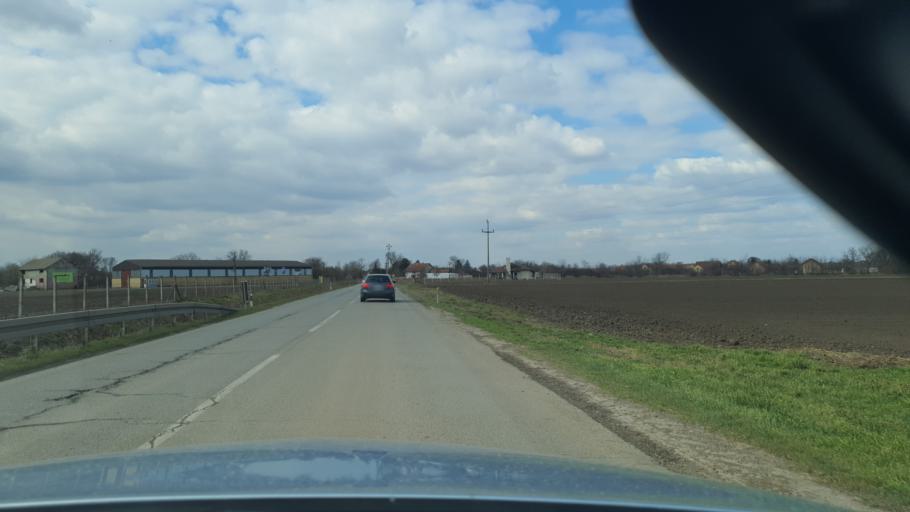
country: RS
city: Maglic
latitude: 45.3916
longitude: 19.4768
